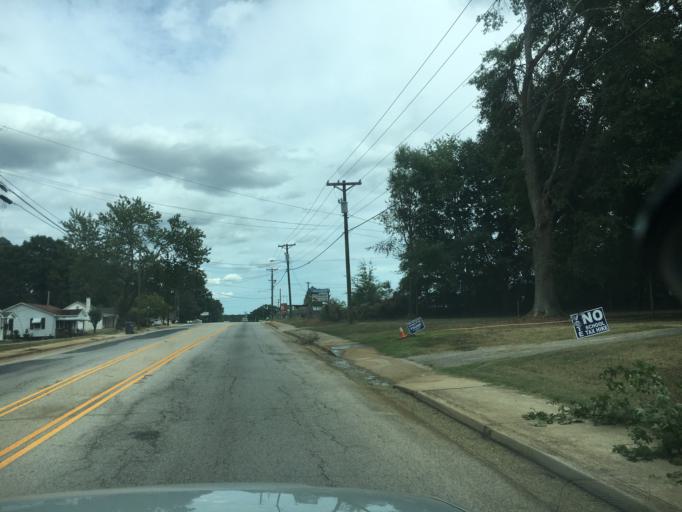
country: US
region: South Carolina
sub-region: Laurens County
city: Laurens
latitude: 34.5039
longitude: -81.9978
